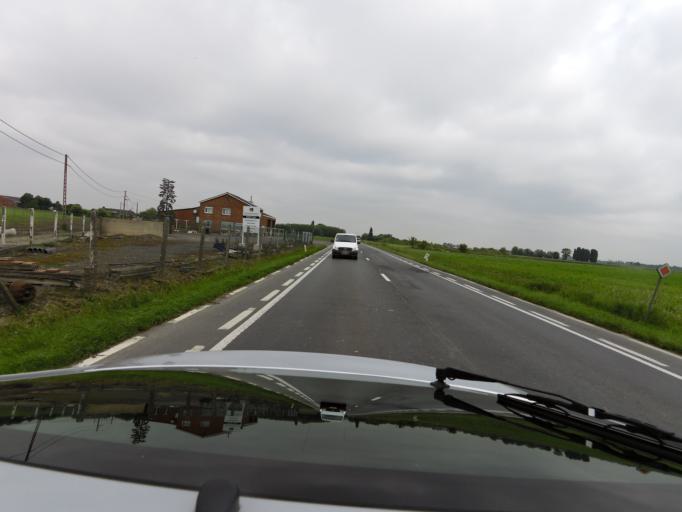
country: BE
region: Flanders
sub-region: Provincie West-Vlaanderen
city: Alveringem
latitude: 51.0175
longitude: 2.6806
